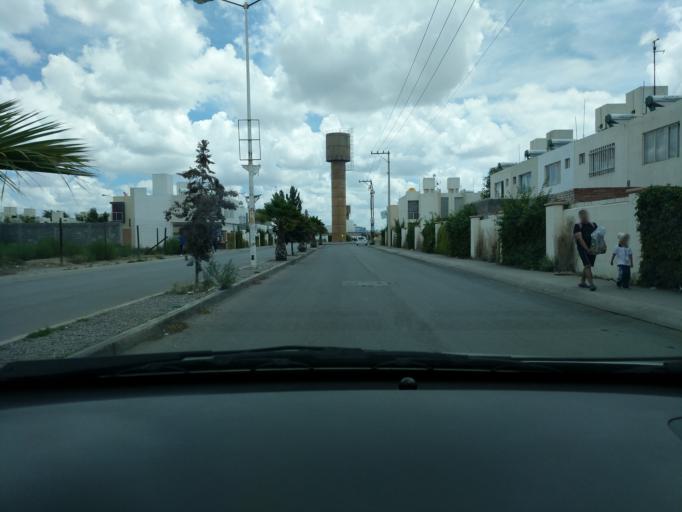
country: MX
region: San Luis Potosi
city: Soledad Diez Gutierrez
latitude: 22.2159
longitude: -100.9369
